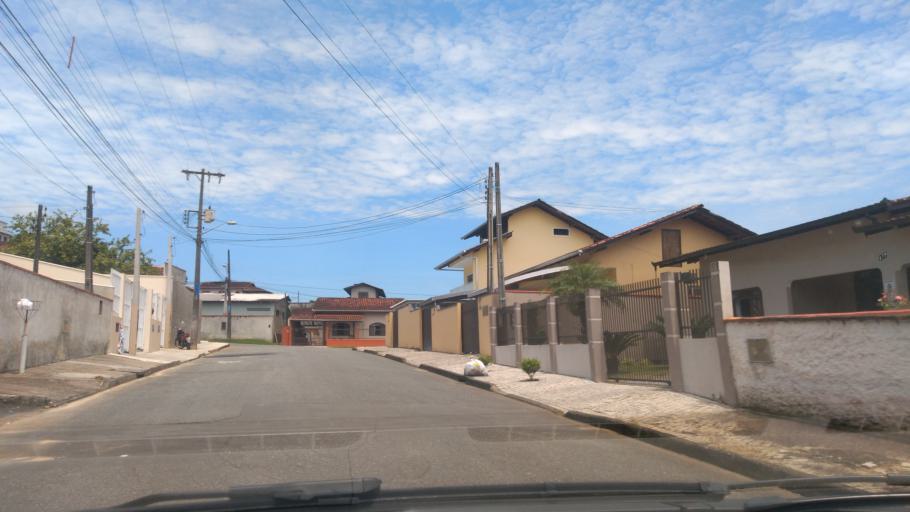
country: BR
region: Santa Catarina
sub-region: Joinville
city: Joinville
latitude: -26.3289
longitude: -48.8071
